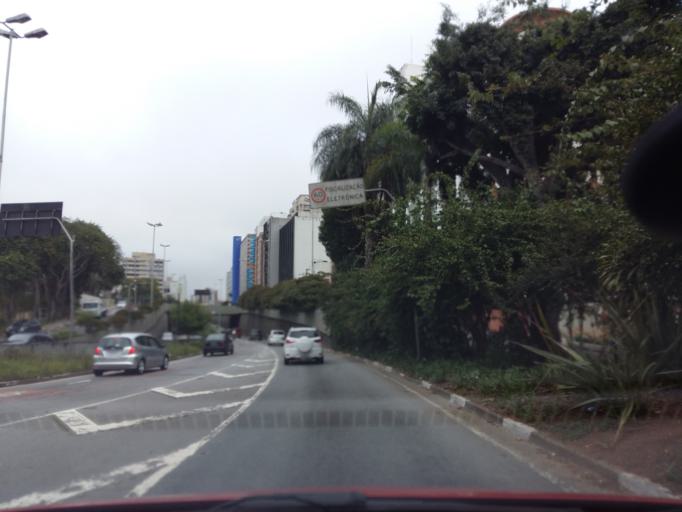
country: BR
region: Sao Paulo
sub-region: Santo Andre
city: Santo Andre
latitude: -23.6577
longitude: -46.5343
